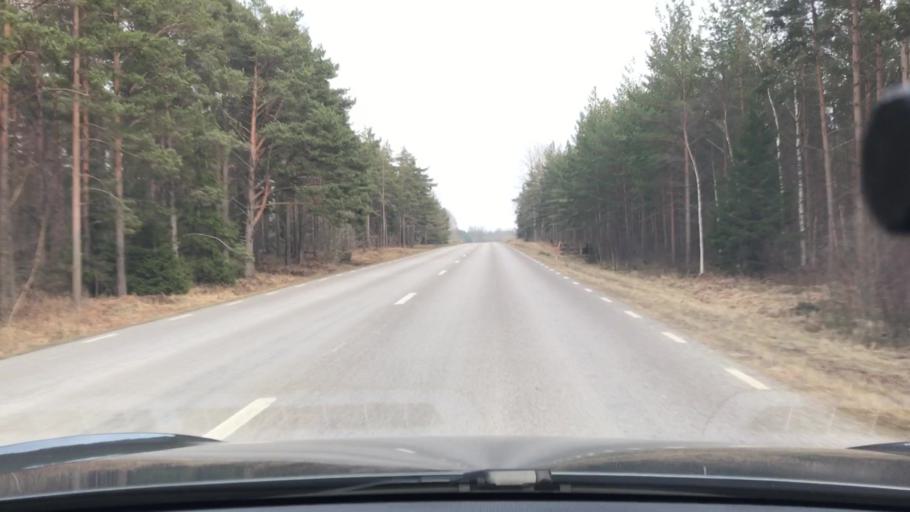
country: SE
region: Gotland
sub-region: Gotland
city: Slite
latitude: 57.4354
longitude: 18.6731
